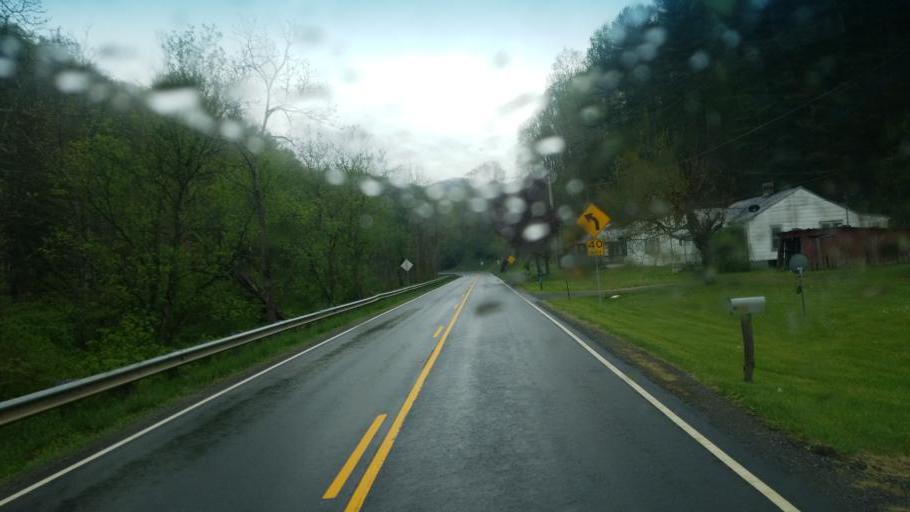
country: US
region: Virginia
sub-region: Smyth County
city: Marion
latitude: 36.8135
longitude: -81.4666
